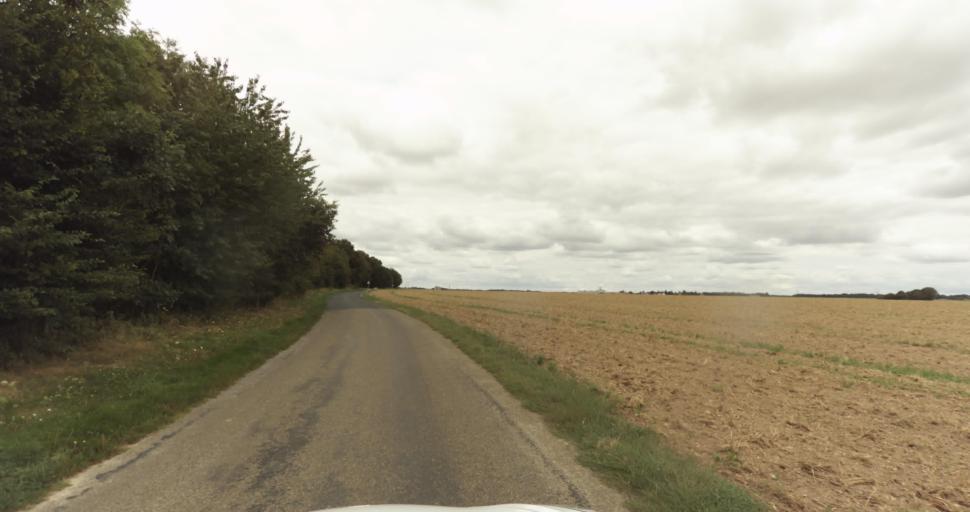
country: FR
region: Haute-Normandie
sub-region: Departement de l'Eure
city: La Madeleine-de-Nonancourt
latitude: 48.8209
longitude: 1.2183
